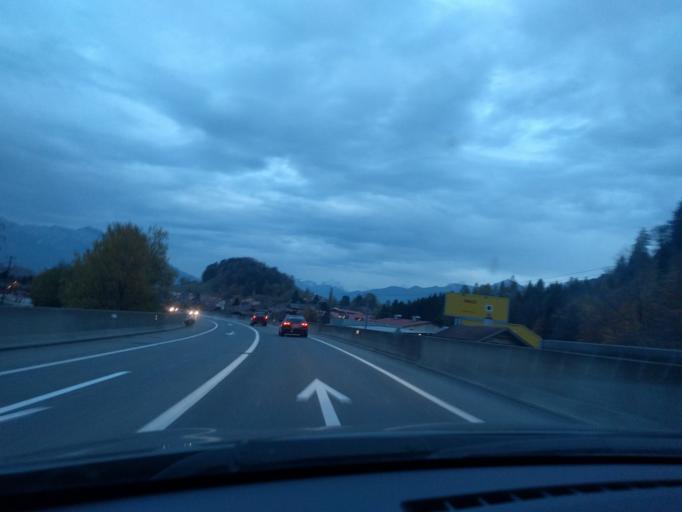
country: CH
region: Bern
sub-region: Frutigen-Niedersimmental District
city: Wimmis
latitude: 46.6749
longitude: 7.6294
